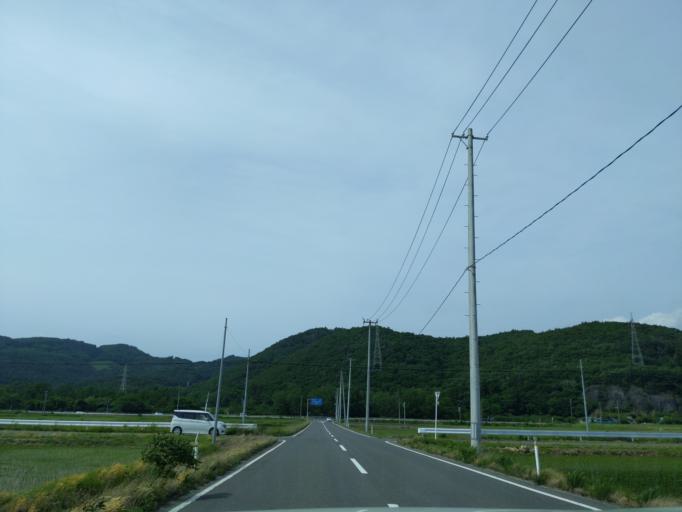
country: JP
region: Fukushima
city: Motomiya
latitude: 37.4748
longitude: 140.3166
